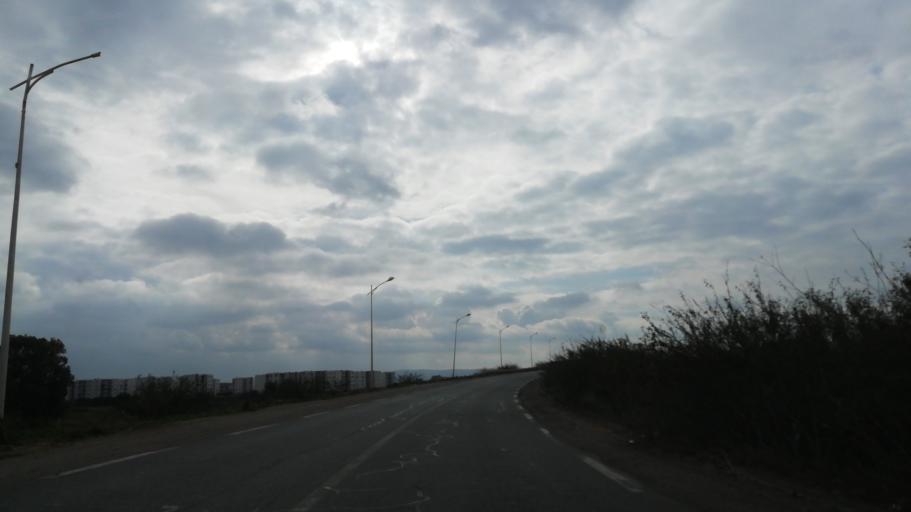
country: DZ
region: Oran
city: Sidi ech Chahmi
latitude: 35.5635
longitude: -0.4465
